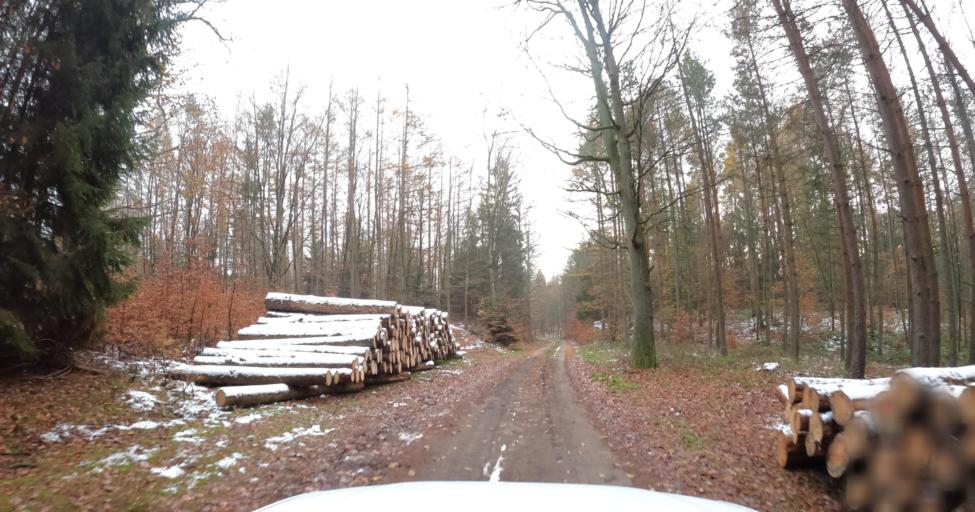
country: PL
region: West Pomeranian Voivodeship
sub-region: Powiat swidwinski
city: Rabino
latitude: 53.9219
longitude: 15.8461
